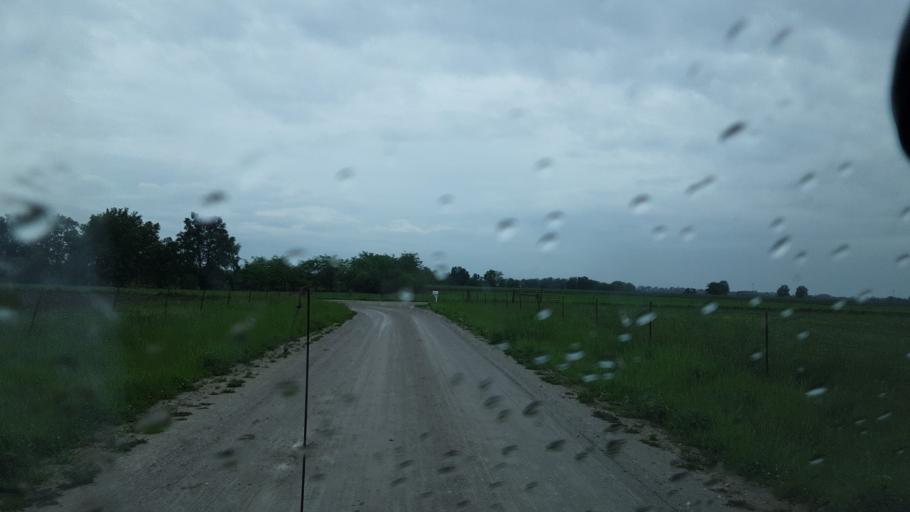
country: US
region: Missouri
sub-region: Randolph County
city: Moberly
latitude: 39.3055
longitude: -92.3054
